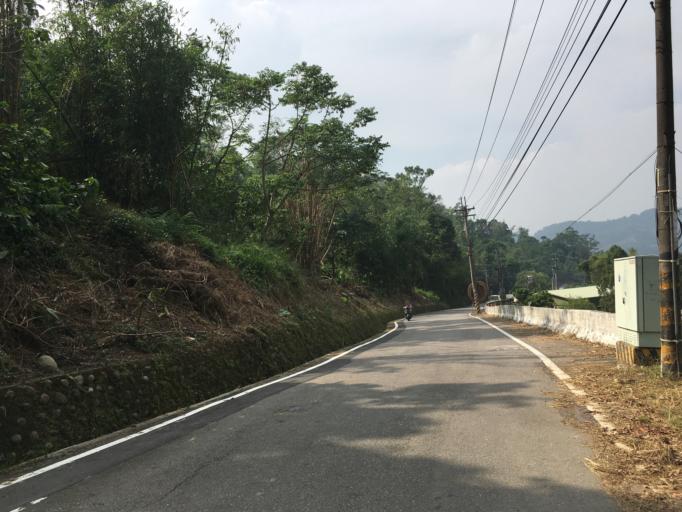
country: TW
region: Taiwan
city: Fengyuan
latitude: 24.1853
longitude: 120.7577
